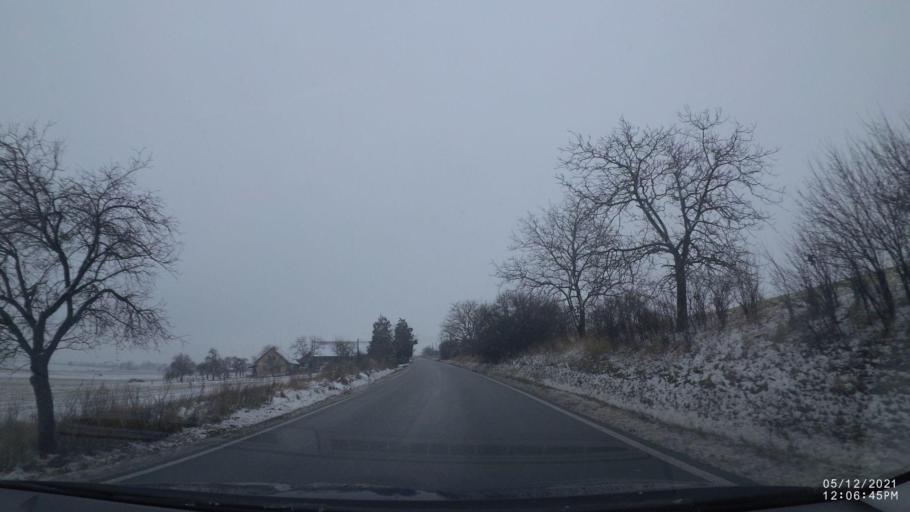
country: CZ
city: Ceske Mezirici
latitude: 50.2949
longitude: 16.0203
